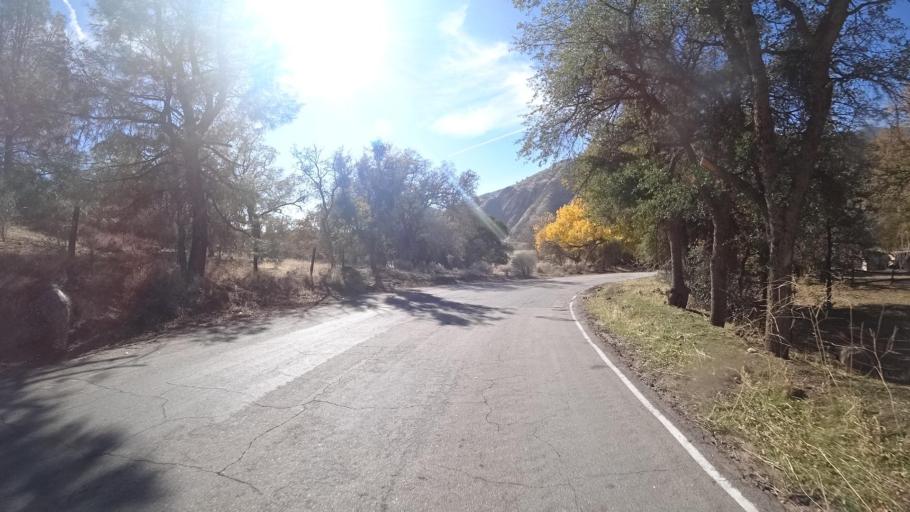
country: US
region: California
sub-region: Kern County
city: Bodfish
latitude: 35.5445
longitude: -118.5073
